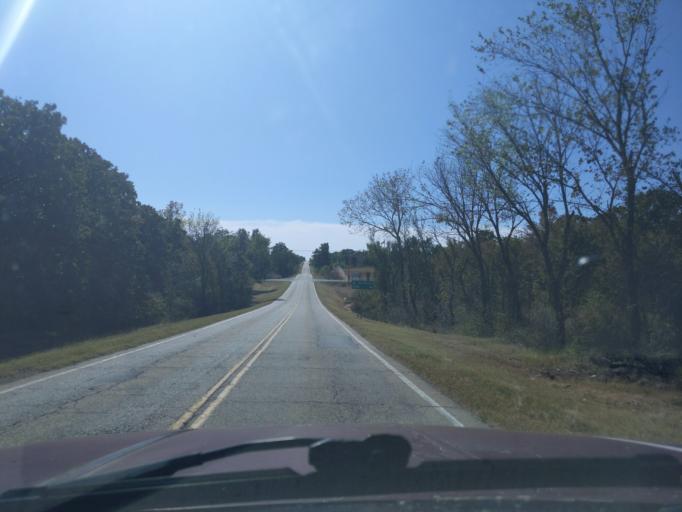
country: US
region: Oklahoma
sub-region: Creek County
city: Bristow
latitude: 35.7136
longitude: -96.3873
